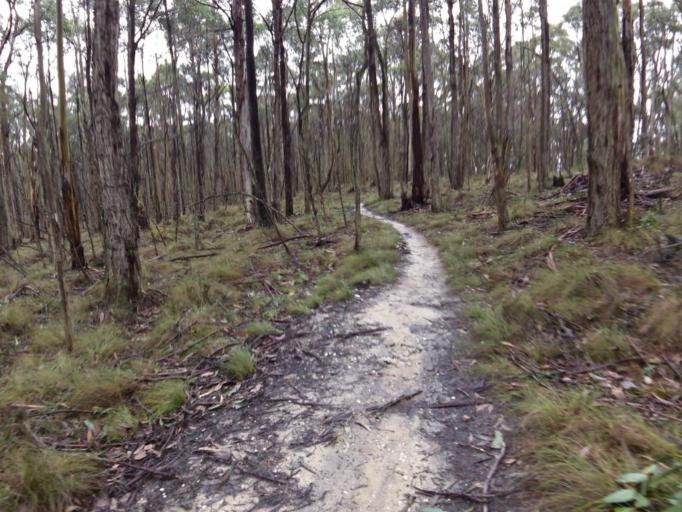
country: AU
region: Victoria
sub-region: Moorabool
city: Bacchus Marsh
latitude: -37.4088
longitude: 144.4904
